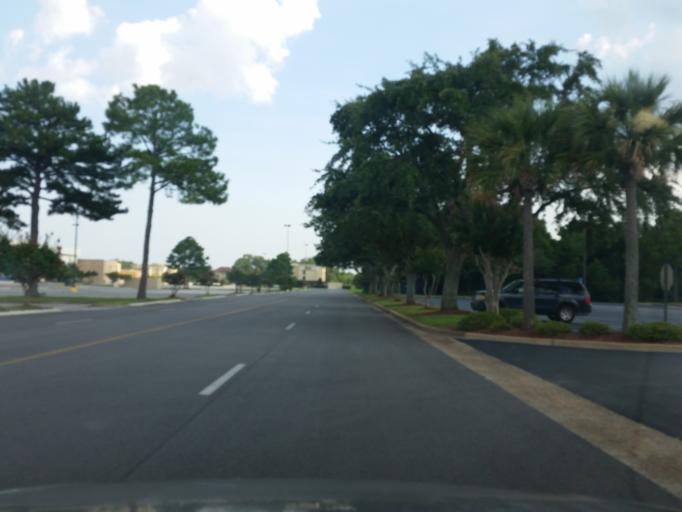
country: US
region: Florida
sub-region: Escambia County
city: Ferry Pass
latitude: 30.5007
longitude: -87.2264
